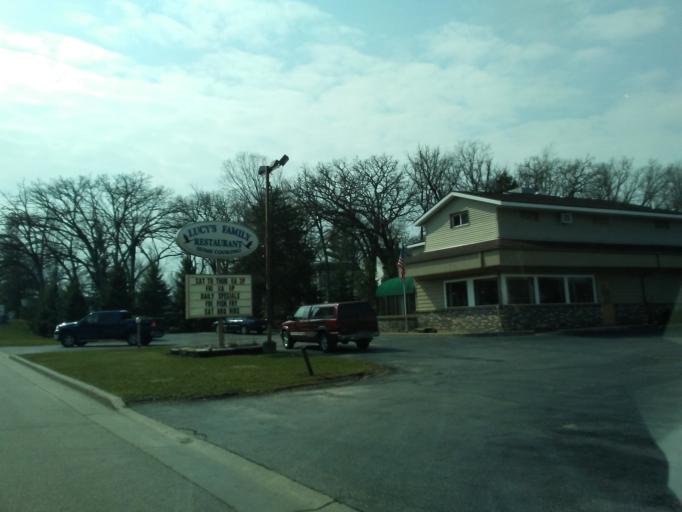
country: US
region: Wisconsin
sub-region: Columbia County
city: Lodi
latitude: 43.3085
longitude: -89.5262
